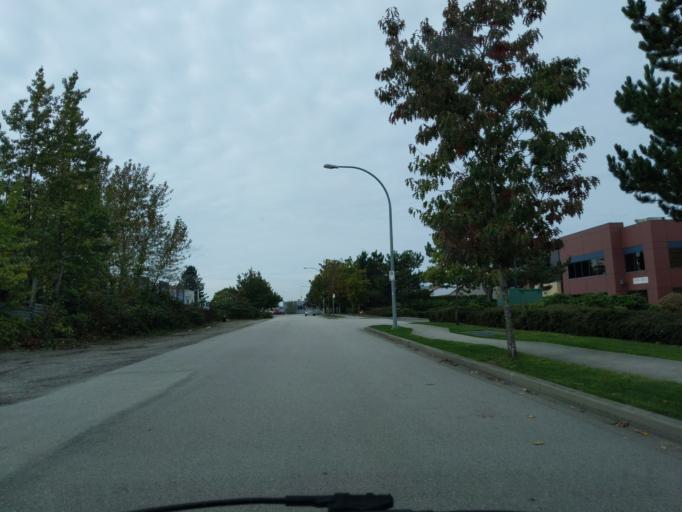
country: CA
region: British Columbia
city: Walnut Grove
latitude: 49.1793
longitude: -122.6616
